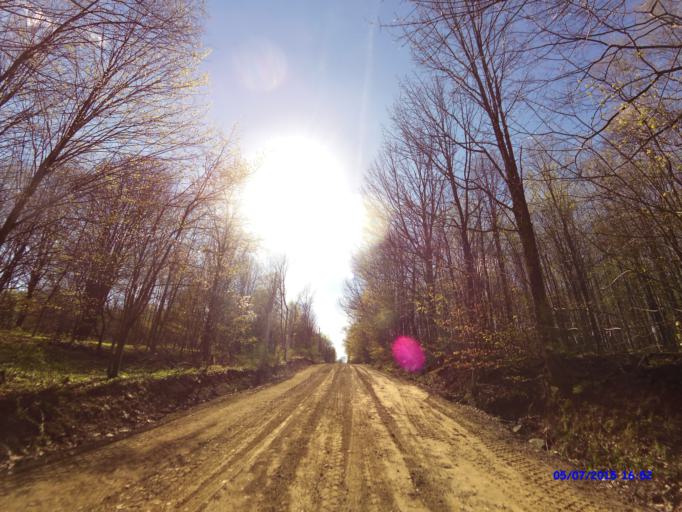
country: US
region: New York
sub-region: Cattaraugus County
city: Little Valley
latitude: 42.2895
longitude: -78.7282
